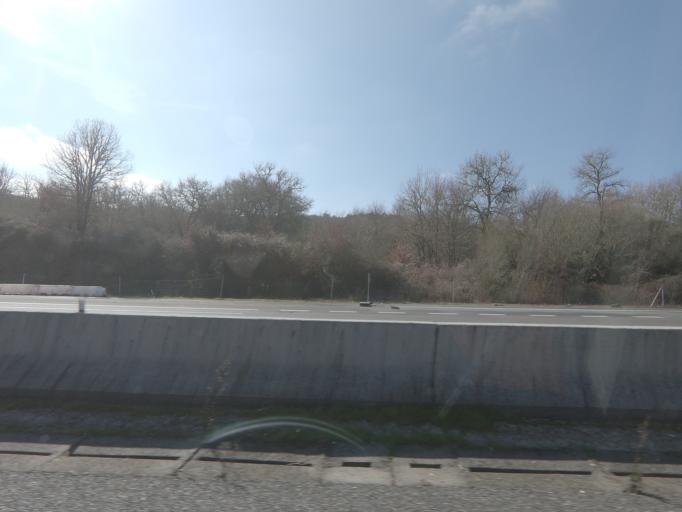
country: ES
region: Galicia
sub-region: Provincia de Ourense
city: Punxin
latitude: 42.3964
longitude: -7.9998
